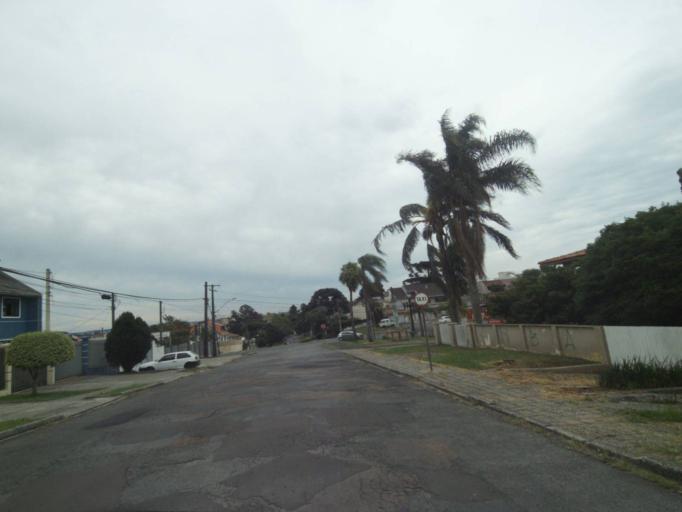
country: BR
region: Parana
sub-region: Pinhais
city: Pinhais
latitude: -25.4137
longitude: -49.2083
